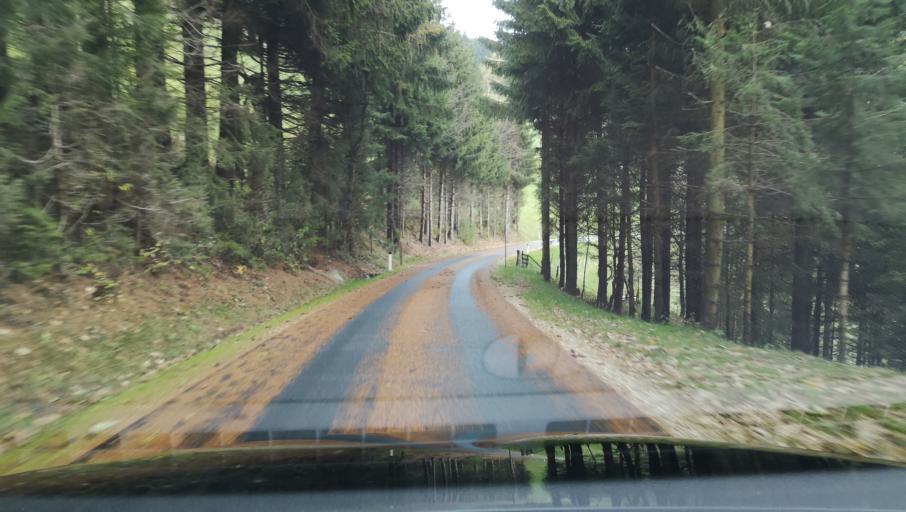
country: AT
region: Styria
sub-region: Politischer Bezirk Weiz
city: Gasen
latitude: 47.3576
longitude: 15.5904
